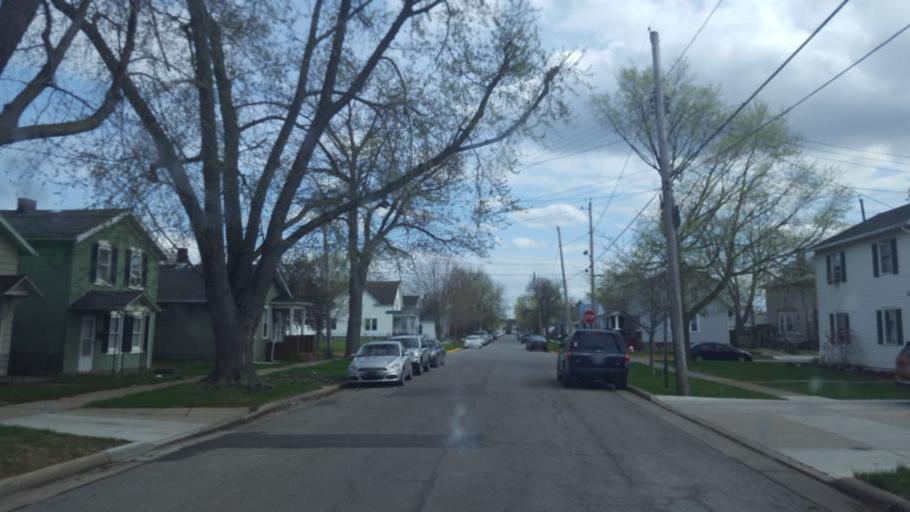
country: US
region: Ohio
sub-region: Erie County
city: Sandusky
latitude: 41.4498
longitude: -82.7192
